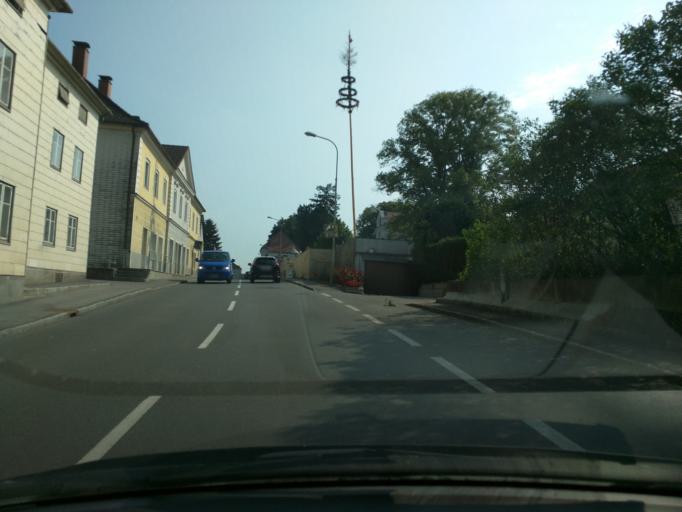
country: AT
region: Lower Austria
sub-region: Politischer Bezirk Melk
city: Ybbs an der Donau
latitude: 48.1540
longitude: 15.0929
